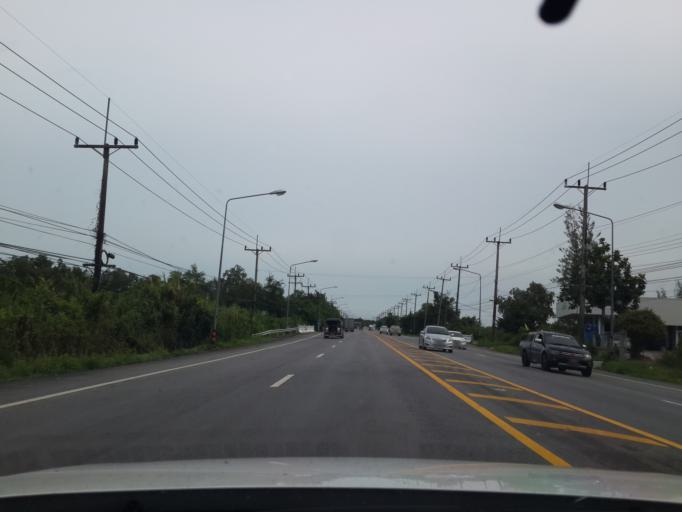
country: TH
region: Pattani
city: Nong Chik
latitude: 6.8269
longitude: 101.1640
